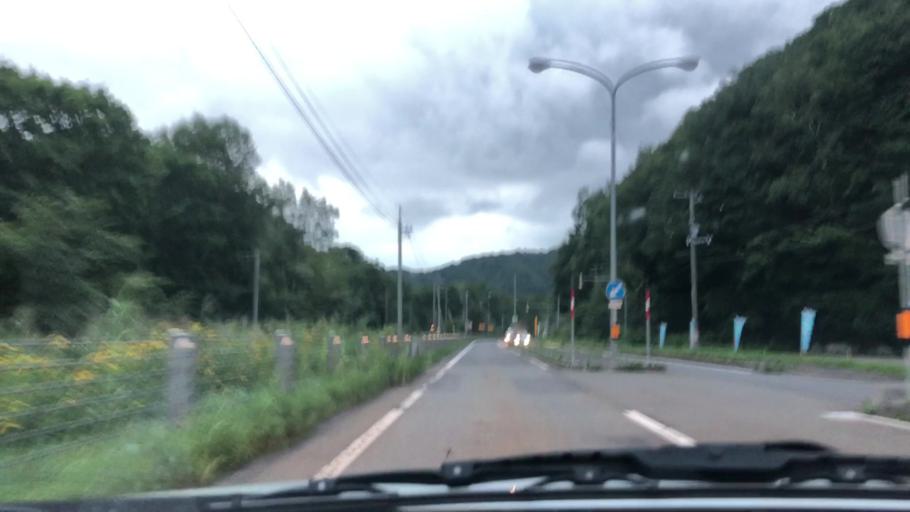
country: JP
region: Hokkaido
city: Chitose
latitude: 42.9132
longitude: 141.9680
